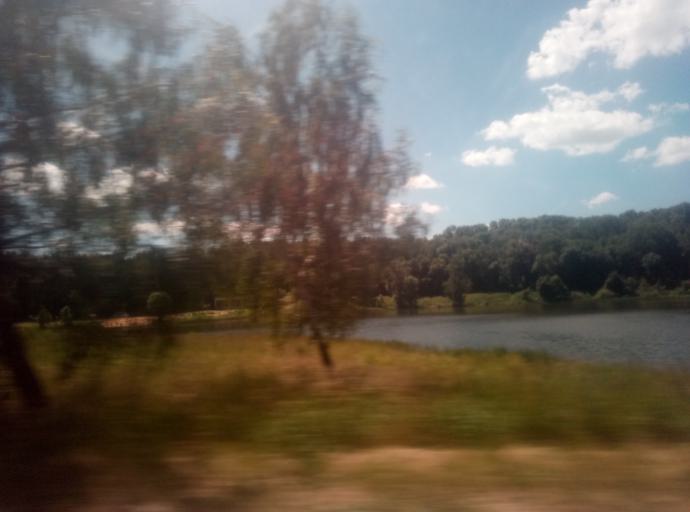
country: RU
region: Tula
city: Kireyevsk
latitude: 53.9326
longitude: 37.9427
